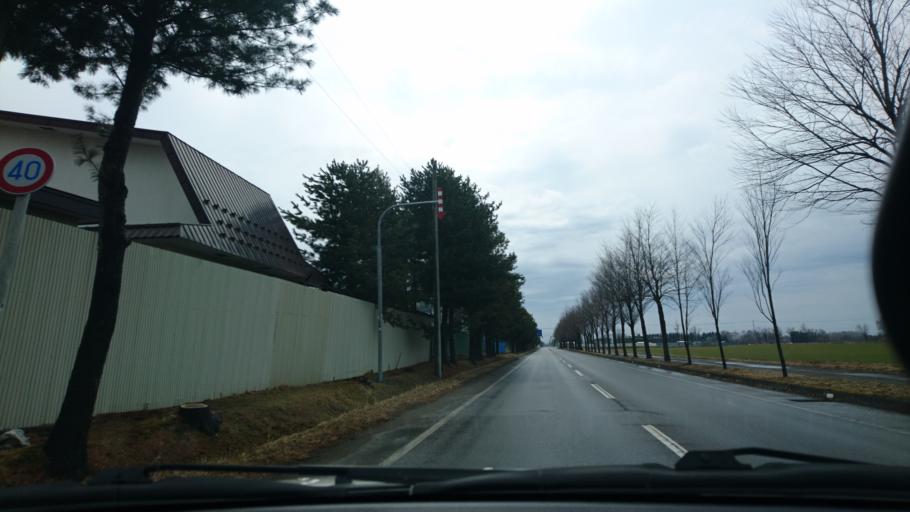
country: JP
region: Hokkaido
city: Otofuke
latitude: 42.9741
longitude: 143.1916
